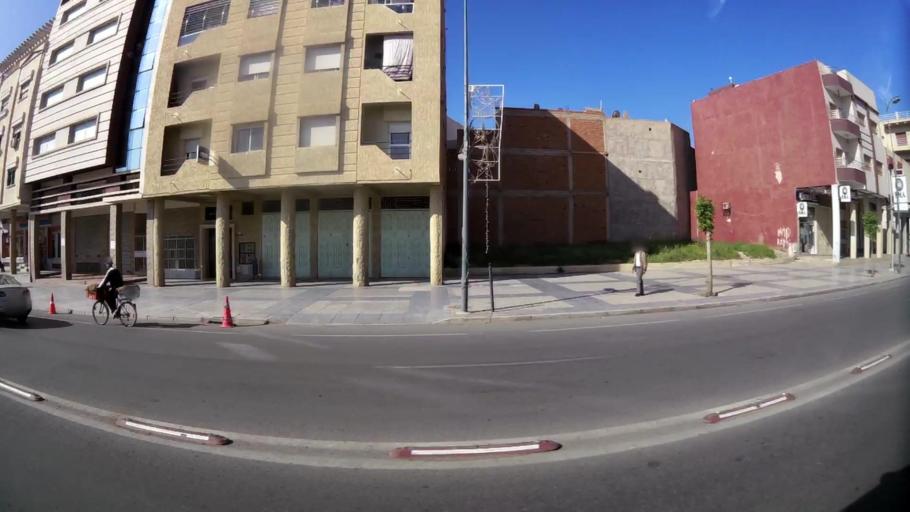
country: MA
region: Oriental
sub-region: Oujda-Angad
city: Oujda
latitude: 34.6800
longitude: -1.9327
